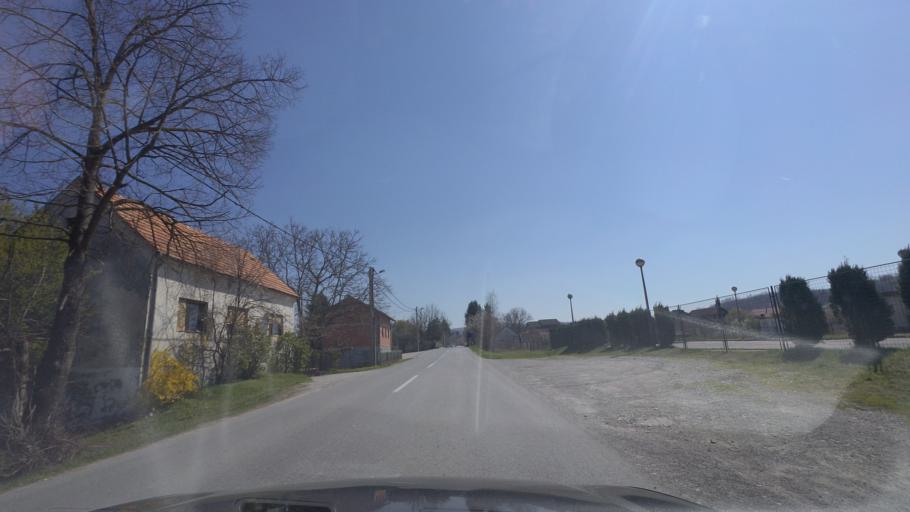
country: HR
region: Karlovacka
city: Vojnic
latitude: 45.3288
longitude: 15.6920
